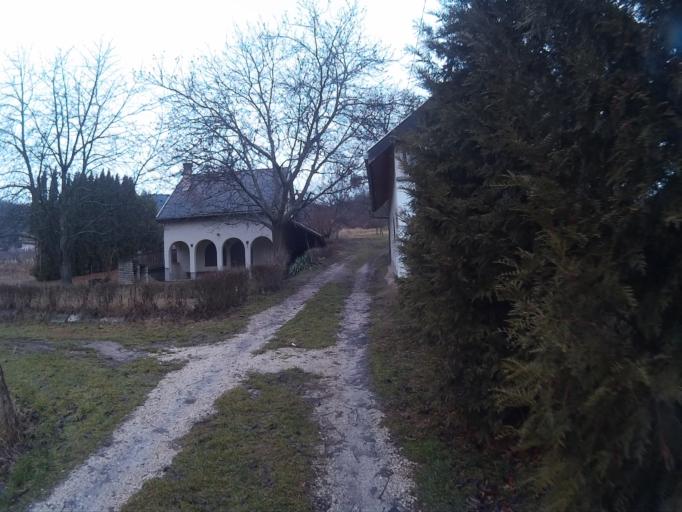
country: HU
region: Komarom-Esztergom
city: Tat
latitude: 47.7198
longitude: 18.6232
